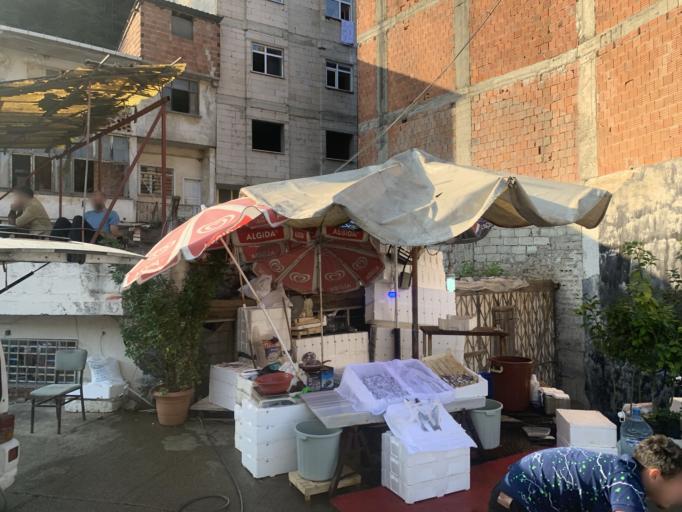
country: TR
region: Trabzon
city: Dernekpazari
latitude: 40.8403
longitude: 40.2795
